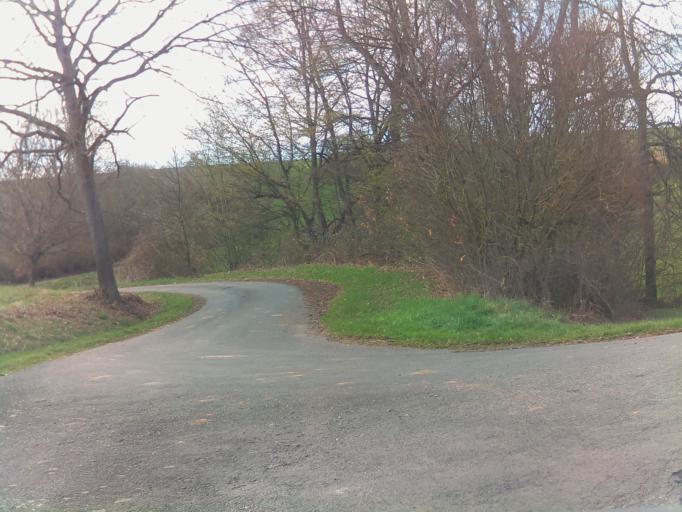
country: DE
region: Rheinland-Pfalz
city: Barenbach
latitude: 49.7448
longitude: 7.4365
